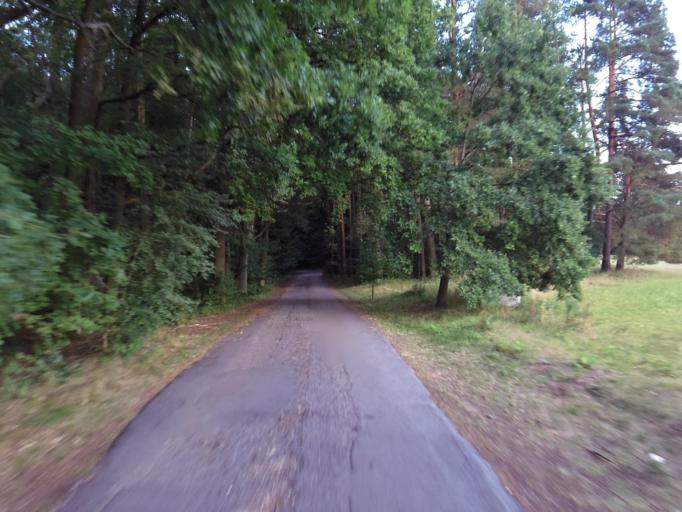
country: CZ
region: Jihocesky
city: Chlum u Trebone
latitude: 48.9848
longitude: 14.9581
